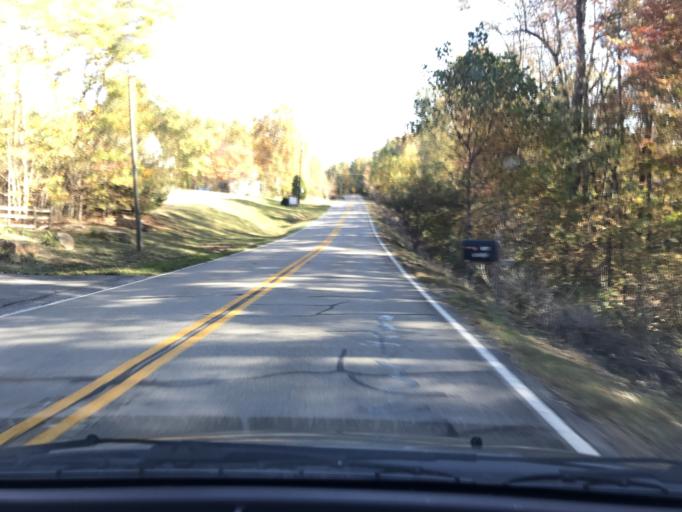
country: US
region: Georgia
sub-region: Dade County
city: Trenton
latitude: 34.8999
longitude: -85.4418
